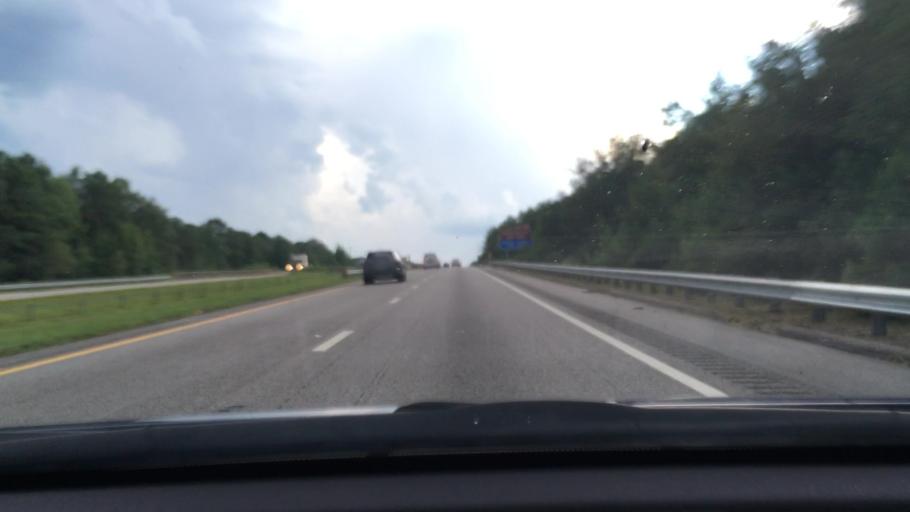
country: US
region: South Carolina
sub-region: Kershaw County
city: Camden
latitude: 34.2161
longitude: -80.5836
